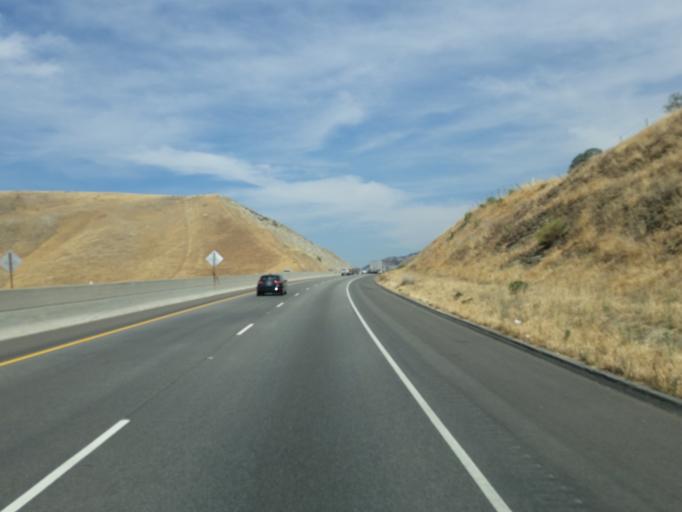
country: US
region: California
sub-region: Kern County
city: Bear Valley Springs
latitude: 35.2697
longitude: -118.6790
